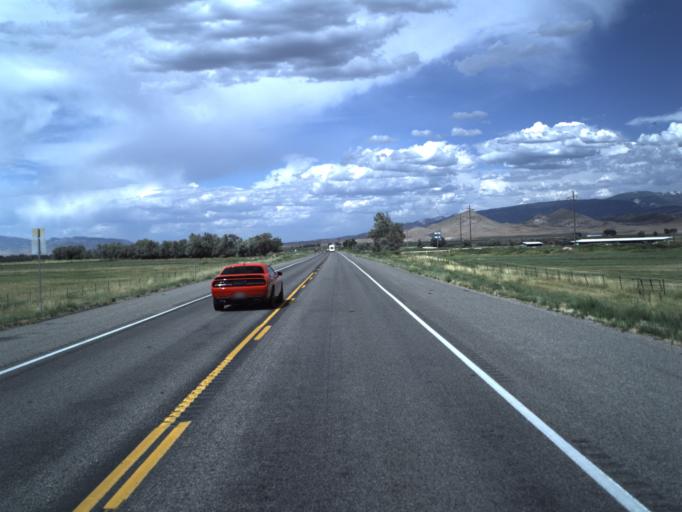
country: US
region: Utah
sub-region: Sevier County
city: Salina
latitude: 38.9754
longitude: -111.8579
